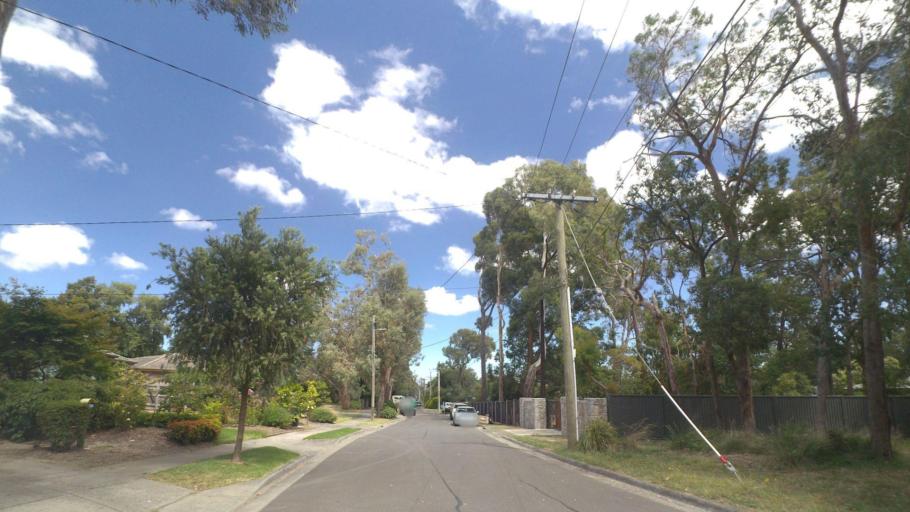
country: AU
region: Victoria
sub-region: Knox
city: Boronia
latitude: -37.8706
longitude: 145.2947
